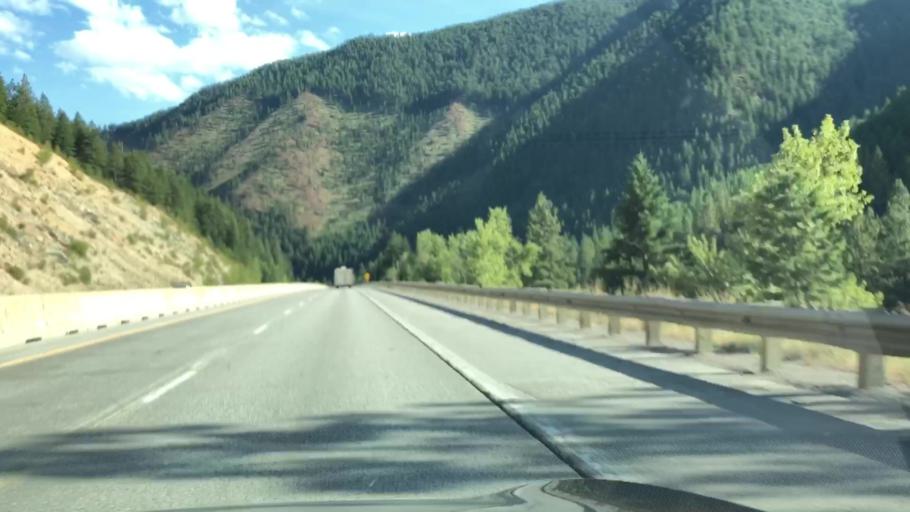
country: US
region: Montana
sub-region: Sanders County
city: Thompson Falls
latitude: 47.3069
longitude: -115.2061
